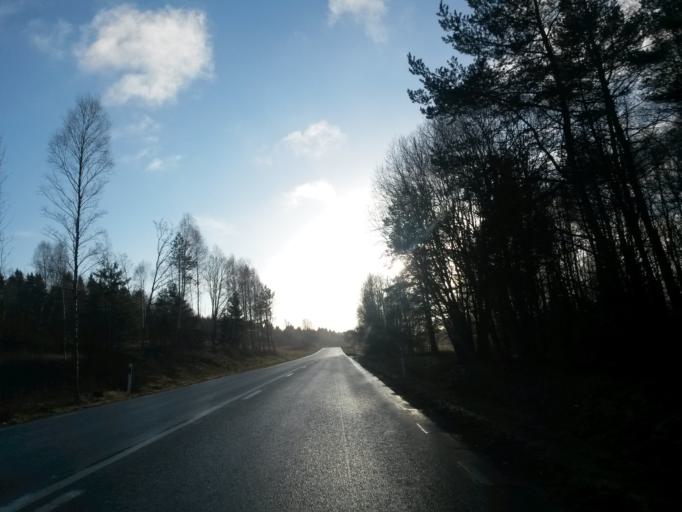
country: SE
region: Vaestra Goetaland
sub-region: Vargarda Kommun
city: Vargarda
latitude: 57.9641
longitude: 12.8136
